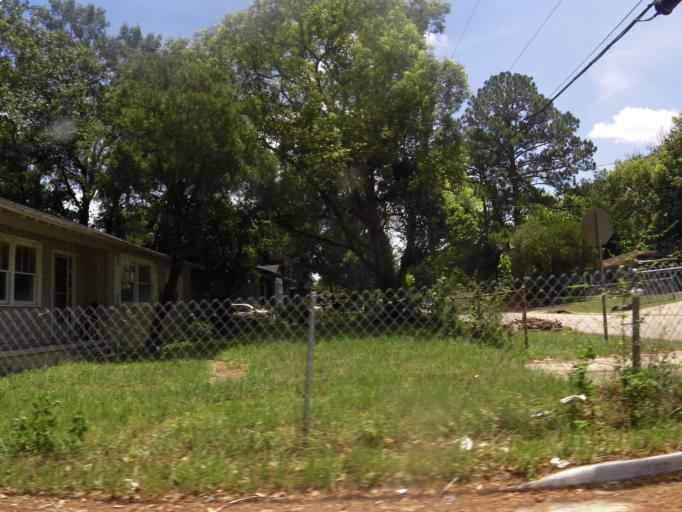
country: US
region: Florida
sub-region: Duval County
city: Jacksonville
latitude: 30.3540
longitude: -81.6970
